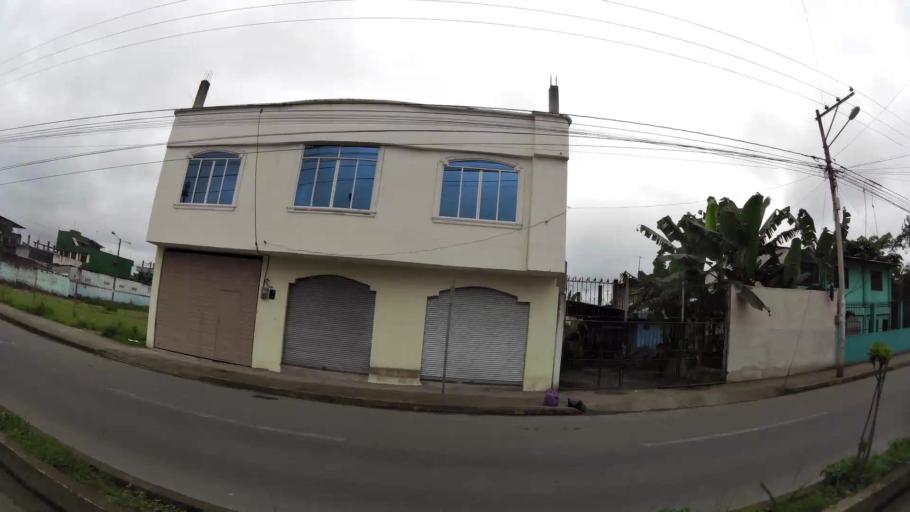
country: EC
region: Santo Domingo de los Tsachilas
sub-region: Canton Santo Domingo de los Colorados
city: Santo Domingo de los Colorados
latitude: -0.2695
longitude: -79.1983
